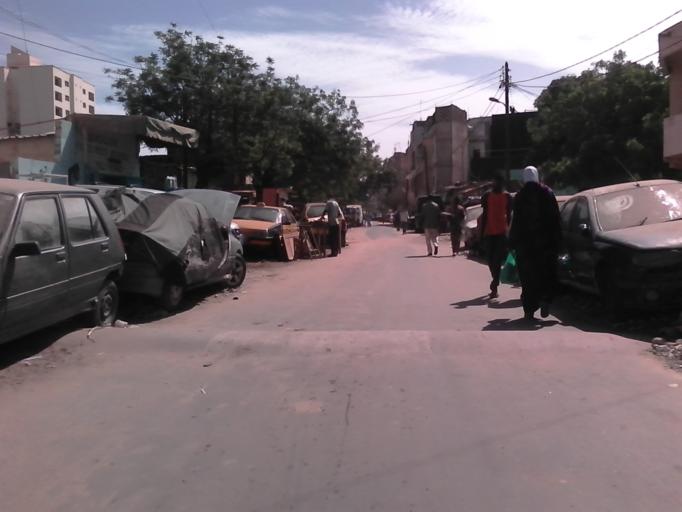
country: SN
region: Dakar
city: Grand Dakar
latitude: 14.7101
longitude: -17.4561
